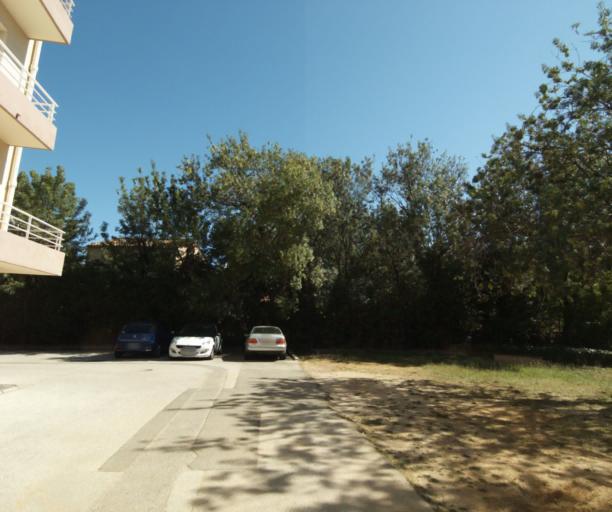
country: FR
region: Provence-Alpes-Cote d'Azur
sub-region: Departement du Var
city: La Garde
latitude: 43.1210
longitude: 6.0075
